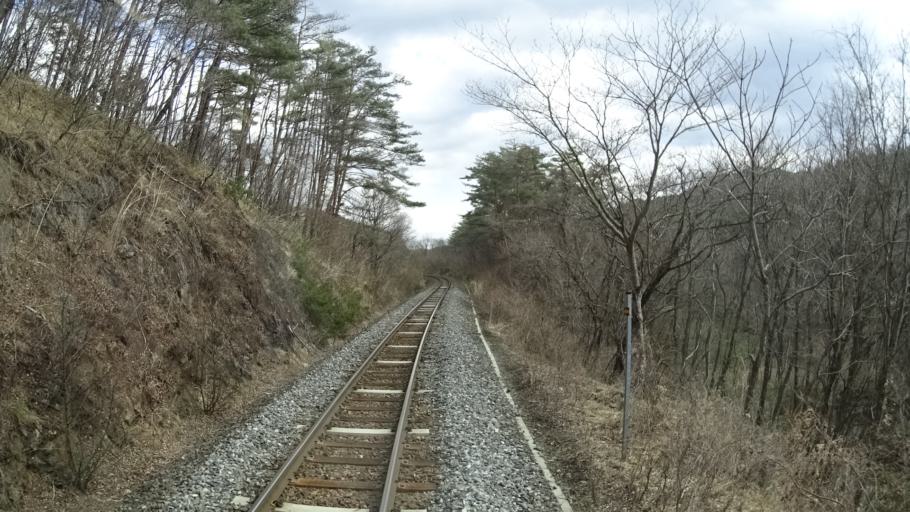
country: JP
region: Iwate
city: Tono
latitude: 39.3350
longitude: 141.3576
